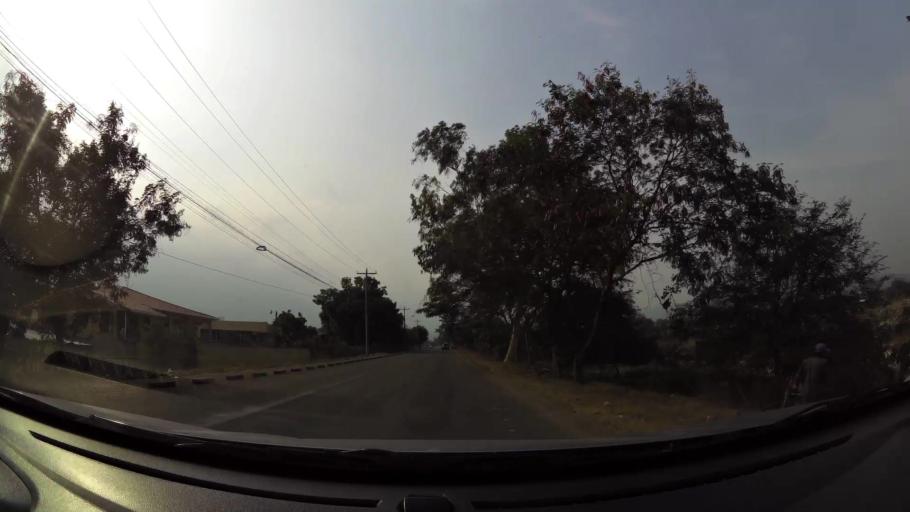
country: HN
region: Cortes
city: San Pedro Sula
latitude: 15.5441
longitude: -88.0077
